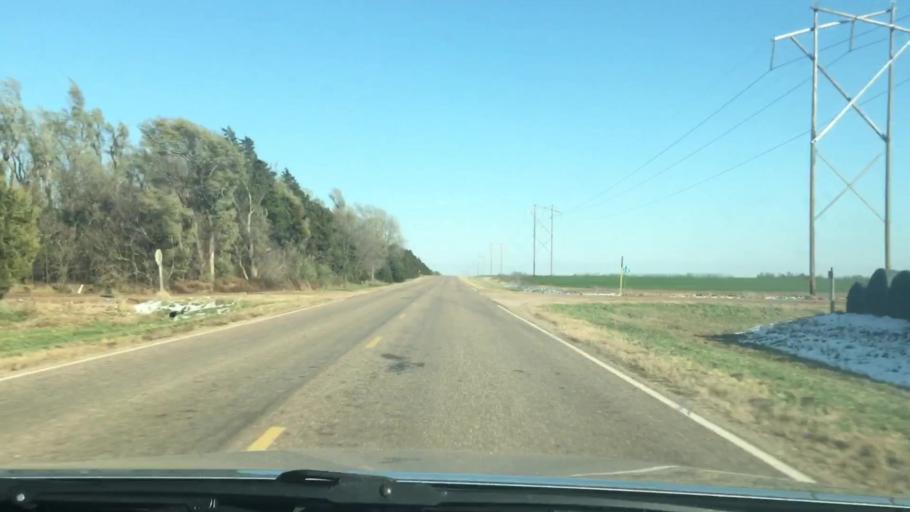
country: US
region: Kansas
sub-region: Rice County
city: Lyons
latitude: 38.2895
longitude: -98.1102
